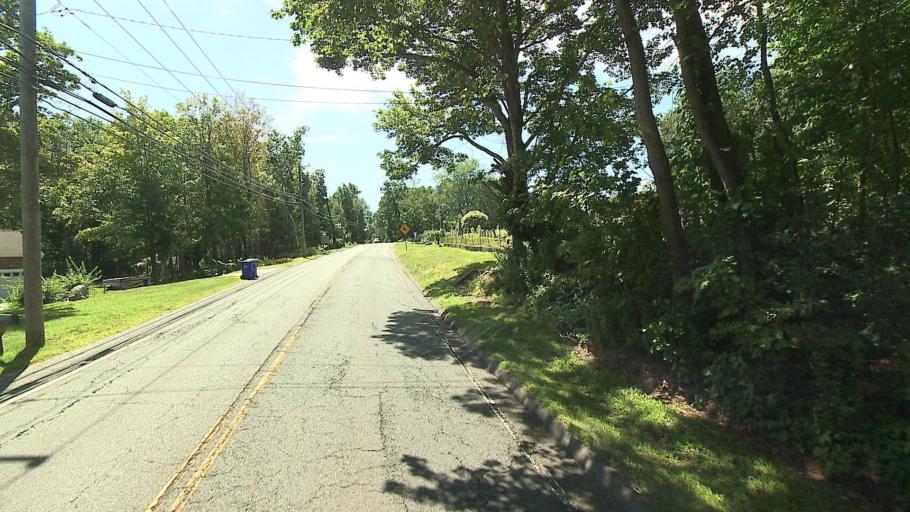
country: US
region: Connecticut
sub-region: Hartford County
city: West Simsbury
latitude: 41.8904
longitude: -72.8932
